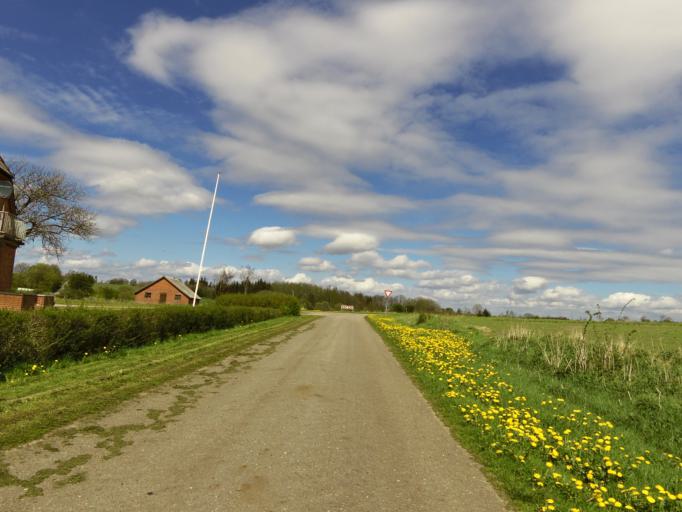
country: DK
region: South Denmark
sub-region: Haderslev Kommune
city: Gram
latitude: 55.2647
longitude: 9.0467
